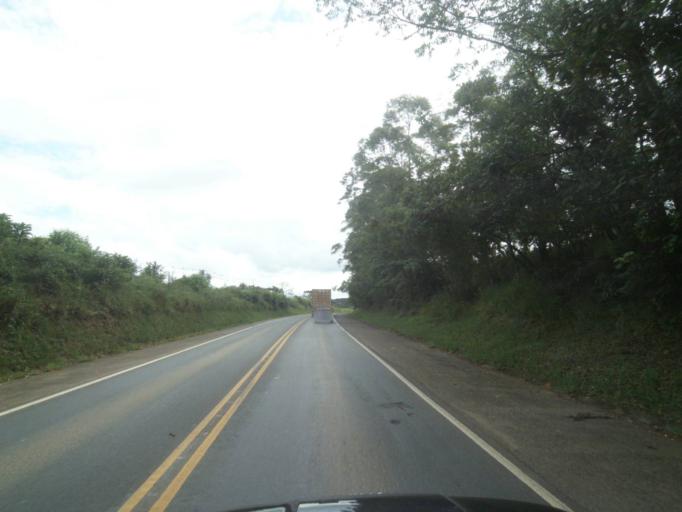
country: BR
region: Parana
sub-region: Telemaco Borba
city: Telemaco Borba
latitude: -24.3675
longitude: -50.6591
